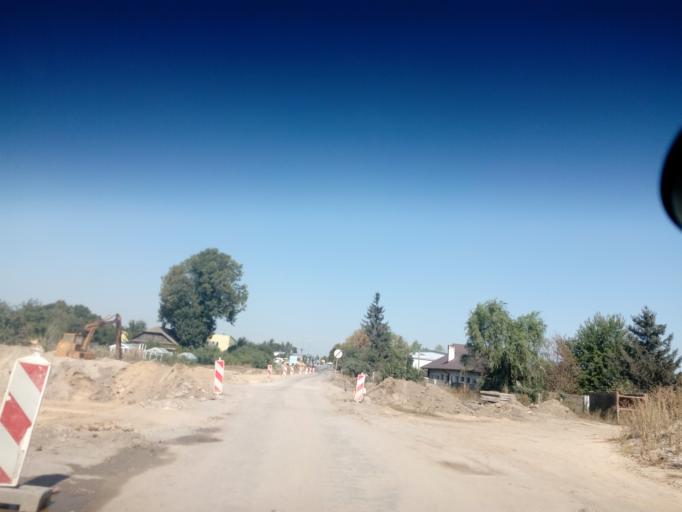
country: PL
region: Lublin Voivodeship
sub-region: Powiat hrubieszowski
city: Hrubieszow
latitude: 50.7893
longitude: 23.9014
